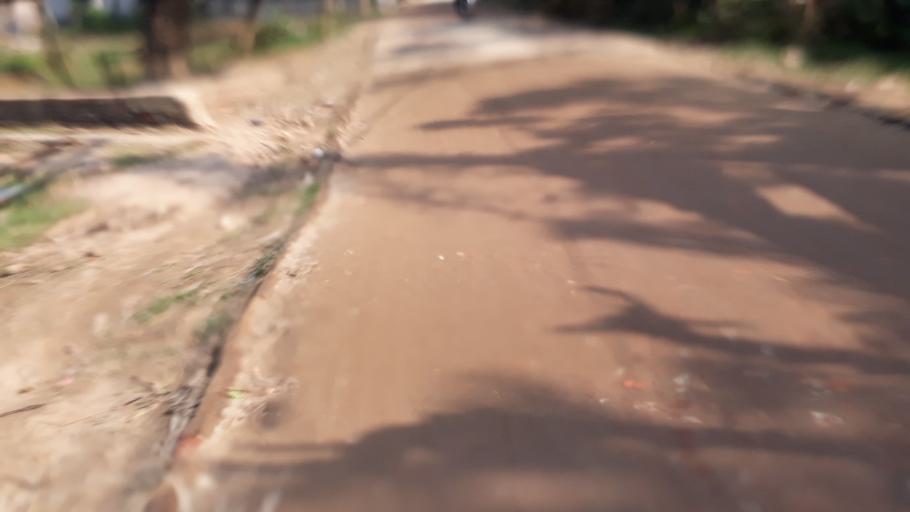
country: BD
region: Dhaka
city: Tungi
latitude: 23.8549
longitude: 90.3031
